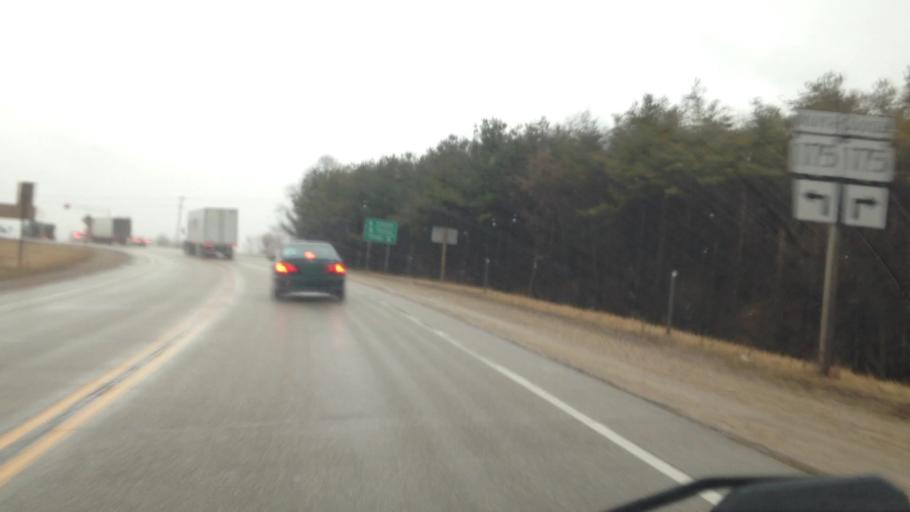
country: US
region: Wisconsin
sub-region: Washington County
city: Hartford
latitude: 43.4214
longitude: -88.3780
